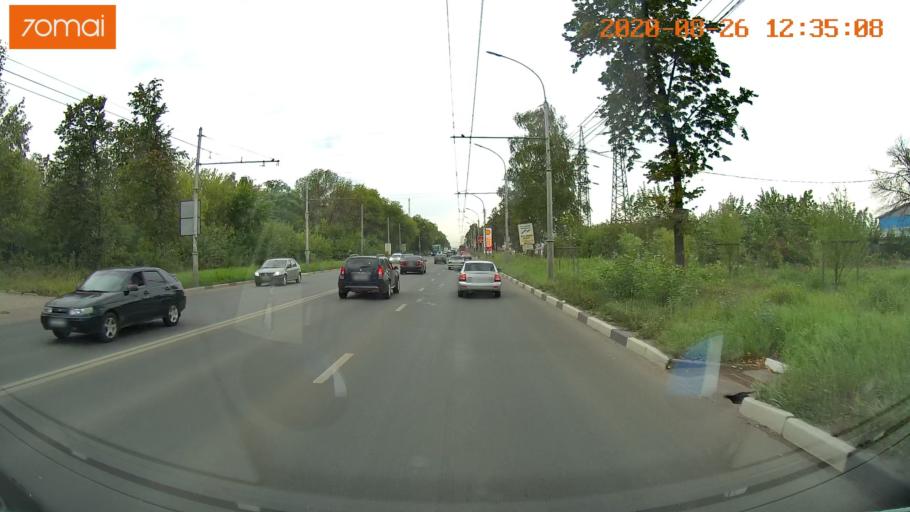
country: RU
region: Rjazan
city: Ryazan'
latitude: 54.5934
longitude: 39.7692
